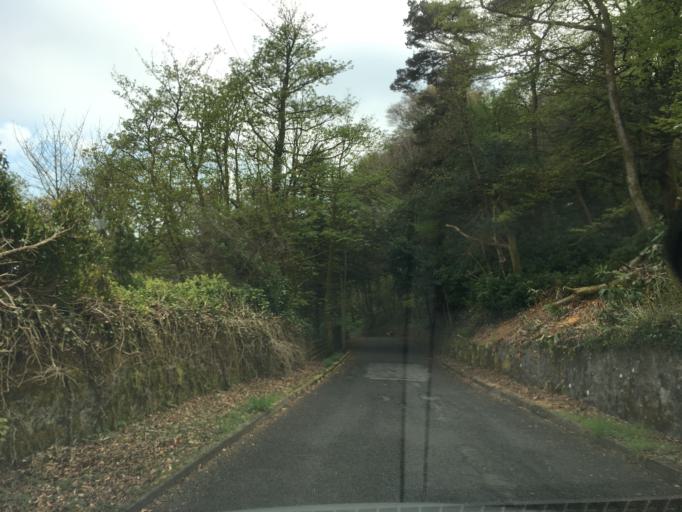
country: GB
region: Scotland
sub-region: Argyll and Bute
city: Rothesay
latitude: 55.8372
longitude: -5.0259
